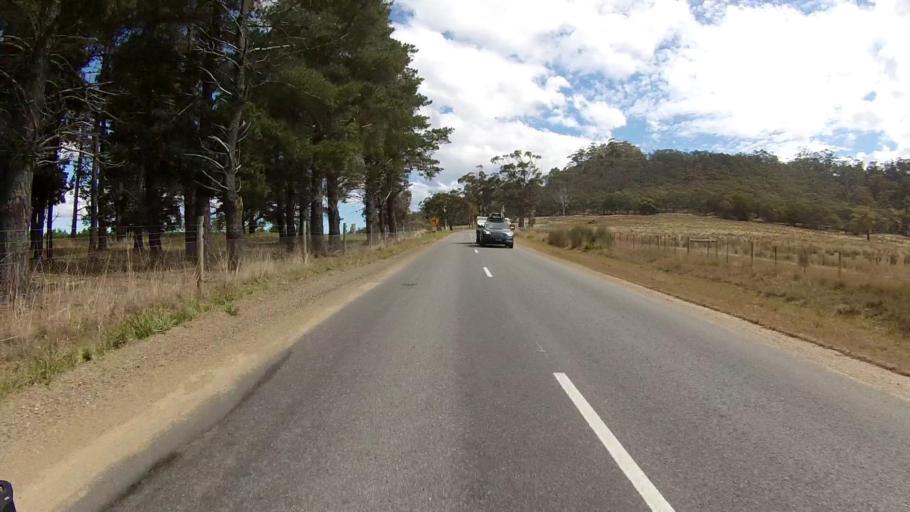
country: AU
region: Tasmania
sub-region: Break O'Day
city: St Helens
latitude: -41.9683
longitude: 148.1525
